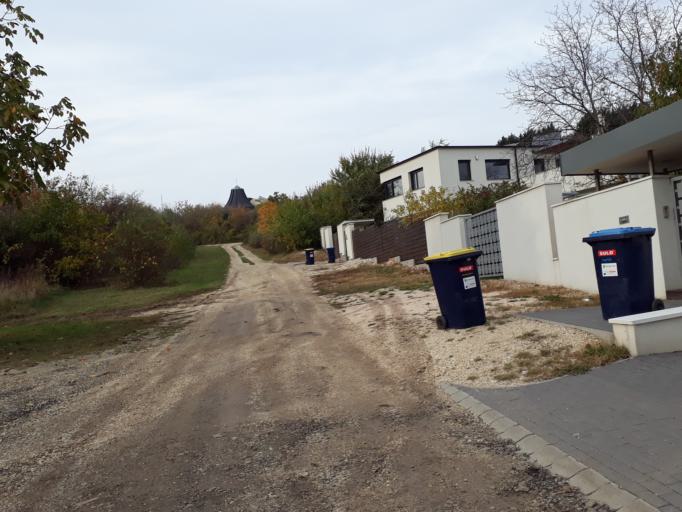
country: HU
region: Budapest
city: Budapest XII. keruelet
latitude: 47.4649
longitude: 18.9974
